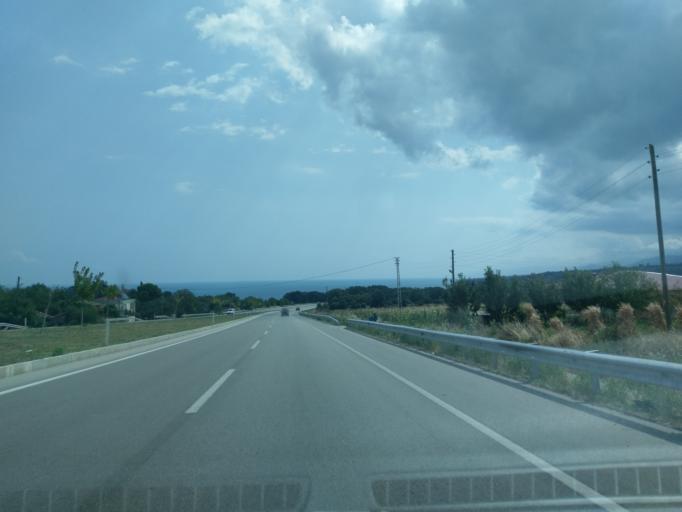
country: TR
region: Sinop
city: Kabali
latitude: 41.8462
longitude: 35.1324
